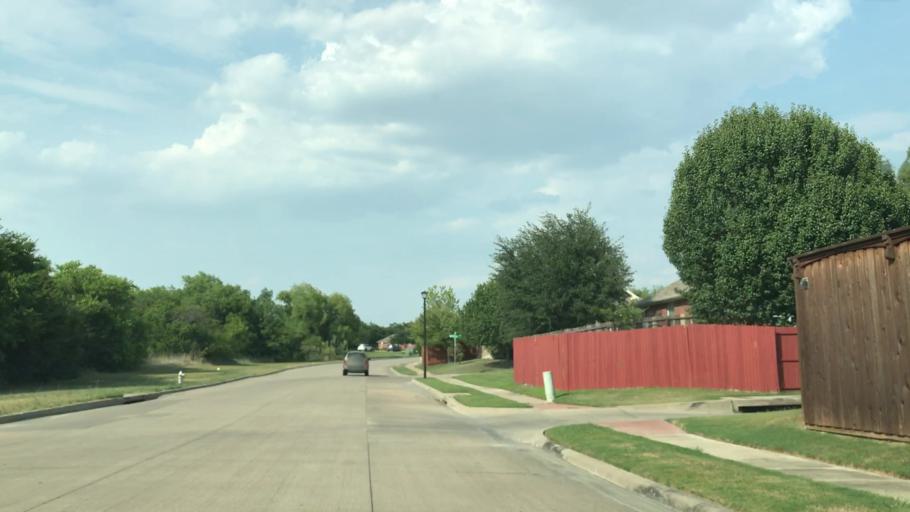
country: US
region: Texas
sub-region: Rockwall County
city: Rockwall
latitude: 32.8979
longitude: -96.4389
